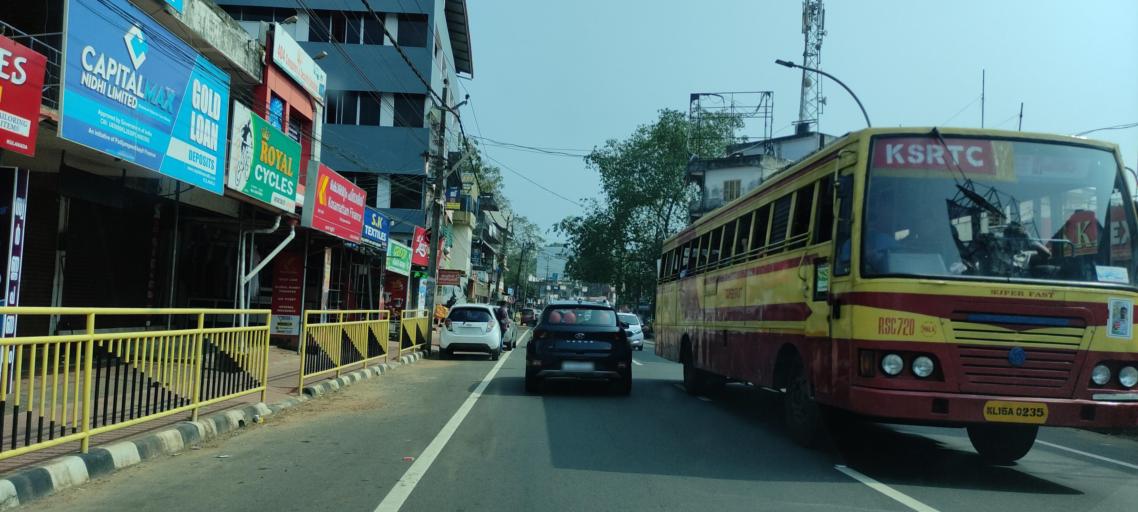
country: IN
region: Kerala
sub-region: Alappuzha
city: Chengannur
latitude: 9.2449
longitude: 76.6708
